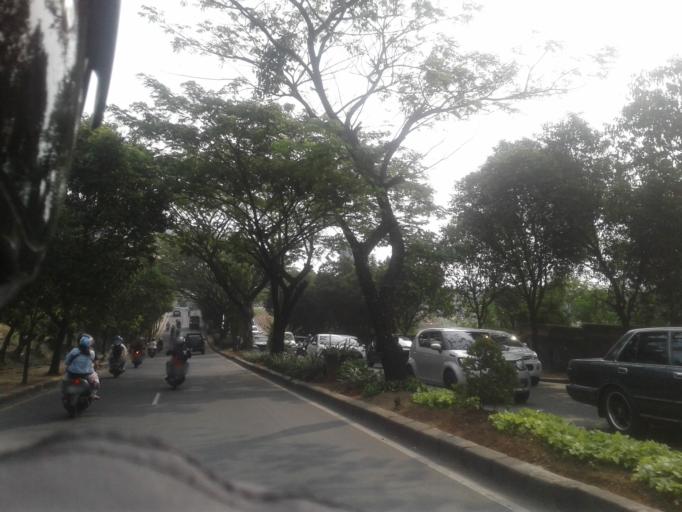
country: ID
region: West Java
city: Depok
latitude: -6.3793
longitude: 106.8466
